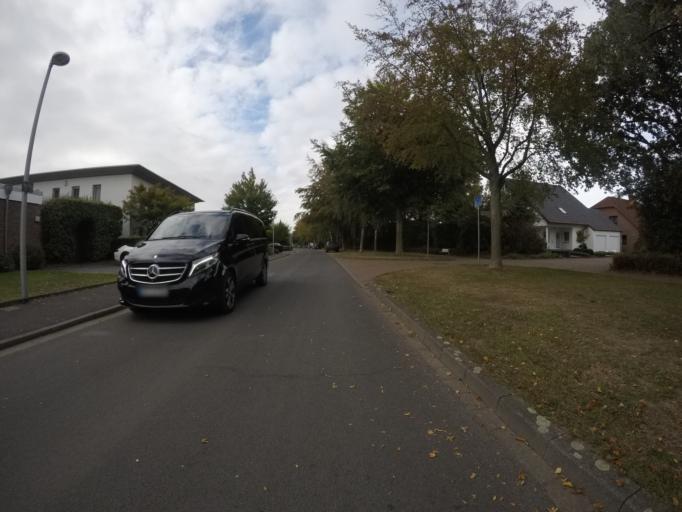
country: DE
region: North Rhine-Westphalia
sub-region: Regierungsbezirk Dusseldorf
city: Bocholt
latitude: 51.8481
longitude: 6.6115
